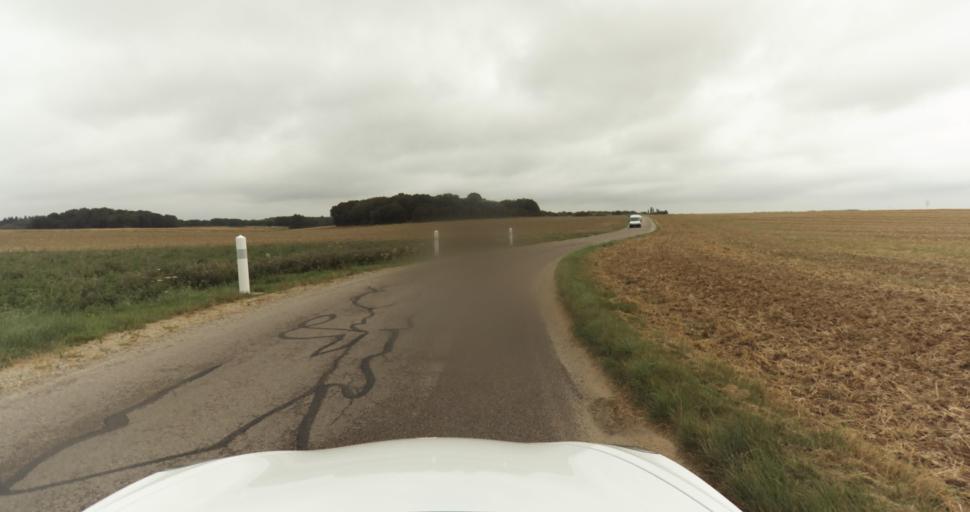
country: FR
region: Haute-Normandie
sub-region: Departement de l'Eure
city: Aviron
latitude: 49.0698
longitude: 1.1042
